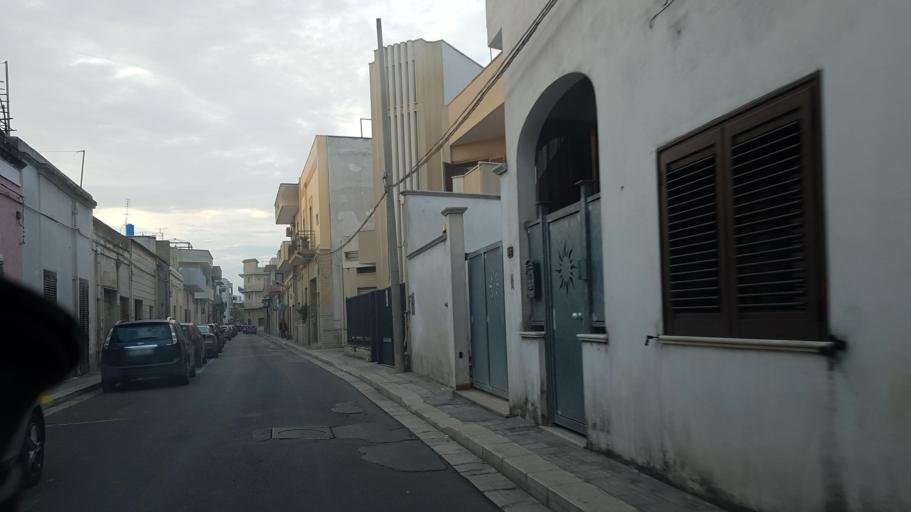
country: IT
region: Apulia
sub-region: Provincia di Brindisi
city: Mesagne
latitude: 40.5566
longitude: 17.8040
